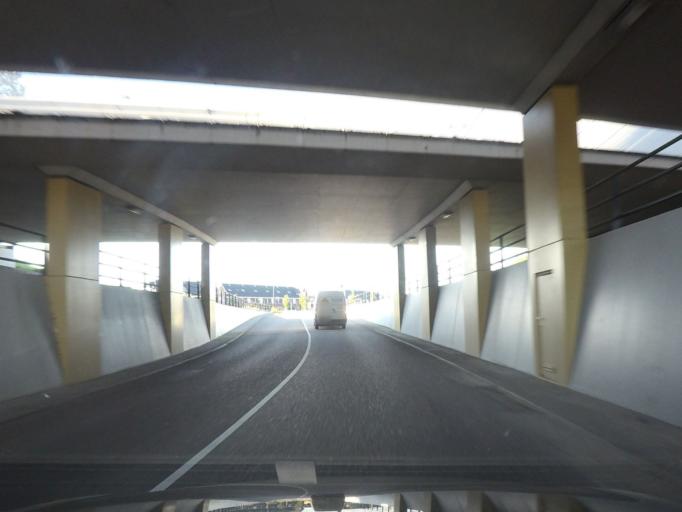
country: NL
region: North Holland
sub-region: Gemeente Beverwijk
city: Beverwijk
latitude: 52.4839
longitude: 4.6770
